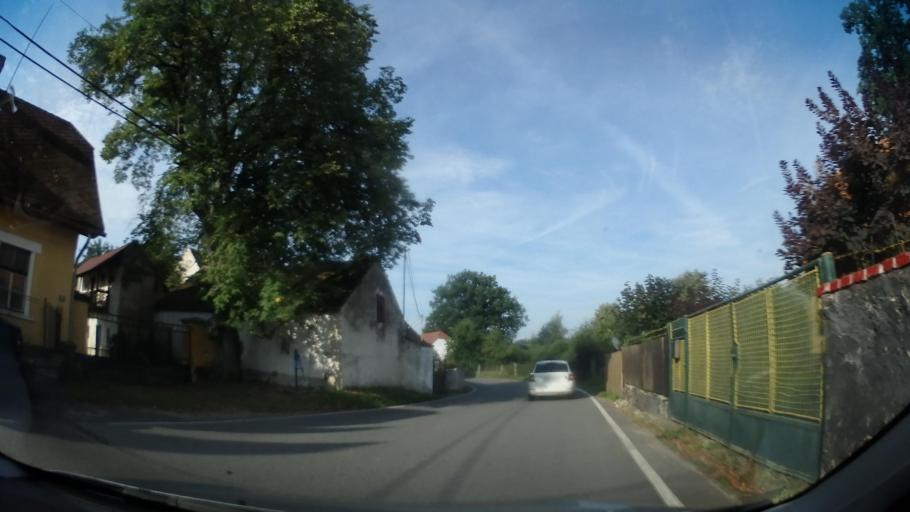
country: CZ
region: Jihocesky
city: Cimelice
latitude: 49.4262
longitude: 14.1210
